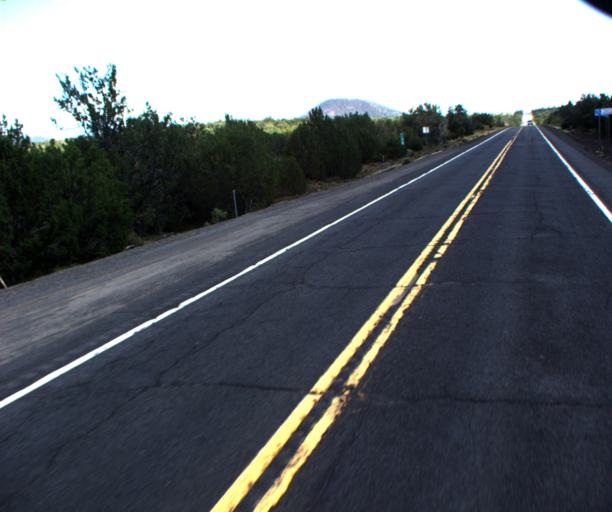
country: US
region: Arizona
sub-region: Coconino County
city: Williams
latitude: 35.4324
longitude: -112.1711
